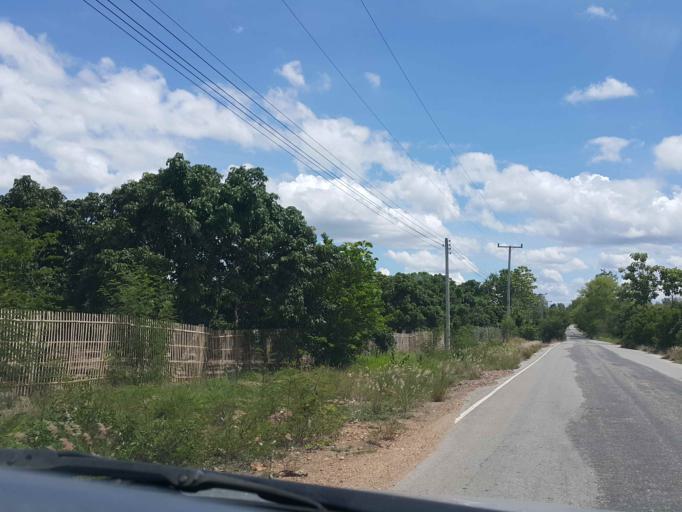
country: TH
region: Chiang Mai
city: Doi Lo
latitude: 18.5099
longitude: 98.7663
